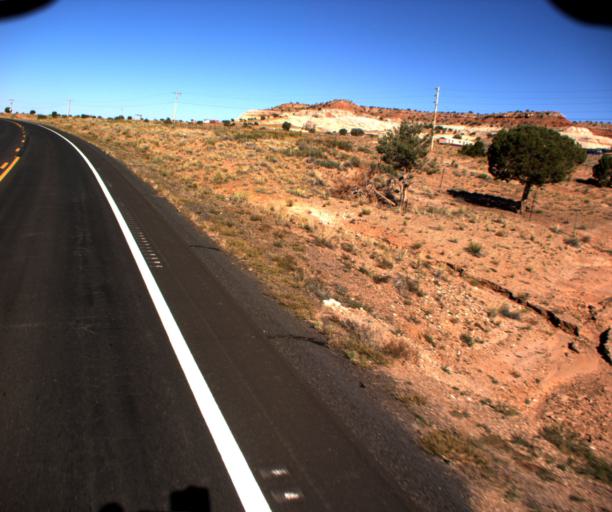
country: US
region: Arizona
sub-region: Coconino County
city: Tuba City
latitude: 36.2368
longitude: -111.0265
